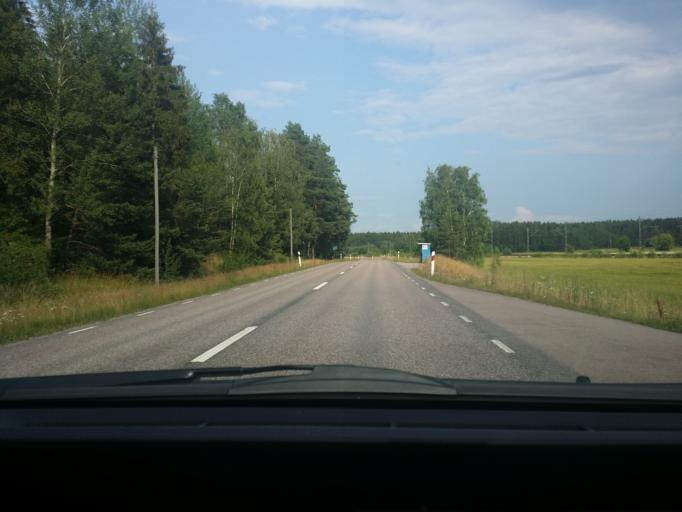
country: SE
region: Vaestmanland
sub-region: Hallstahammars Kommun
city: Kolback
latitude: 59.5662
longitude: 16.3580
